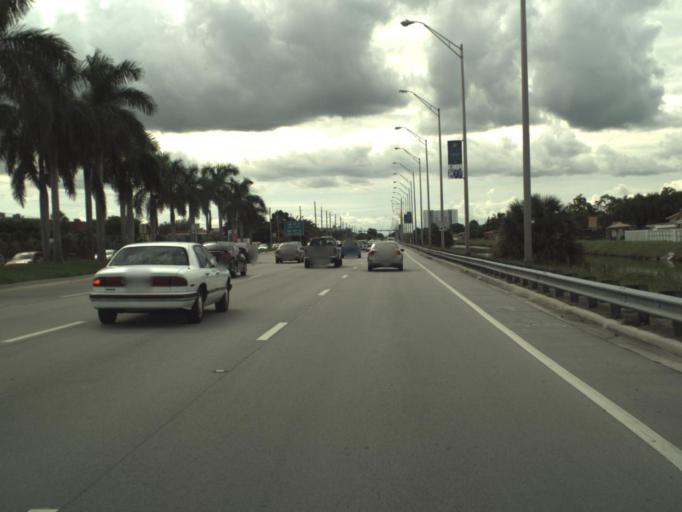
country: US
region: Florida
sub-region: Miami-Dade County
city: Fountainebleau
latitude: 25.7617
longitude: -80.3552
